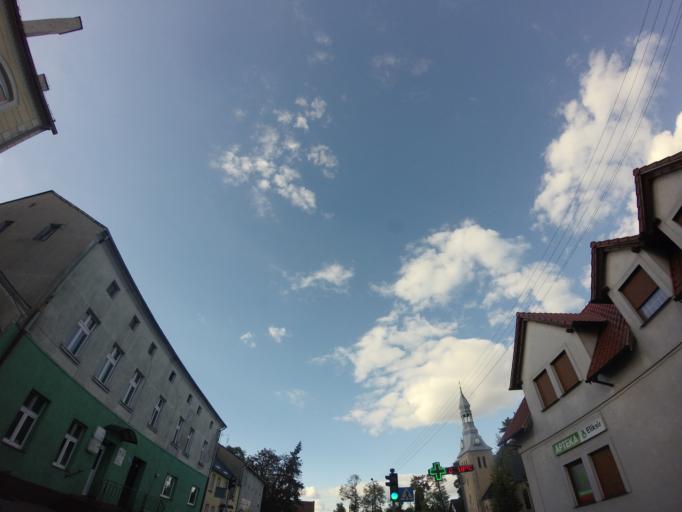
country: PL
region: Greater Poland Voivodeship
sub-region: Powiat nowotomyski
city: Nowy Tomysl
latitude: 52.2676
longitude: 16.1326
